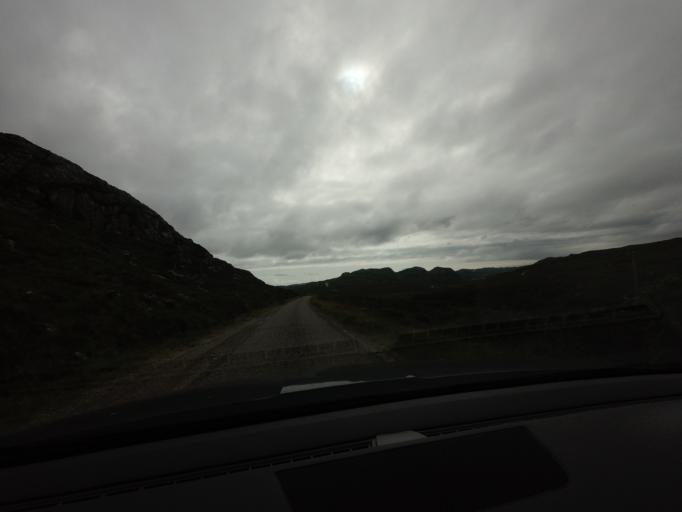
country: GB
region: Scotland
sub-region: Highland
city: Ullapool
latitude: 58.4418
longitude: -4.9554
